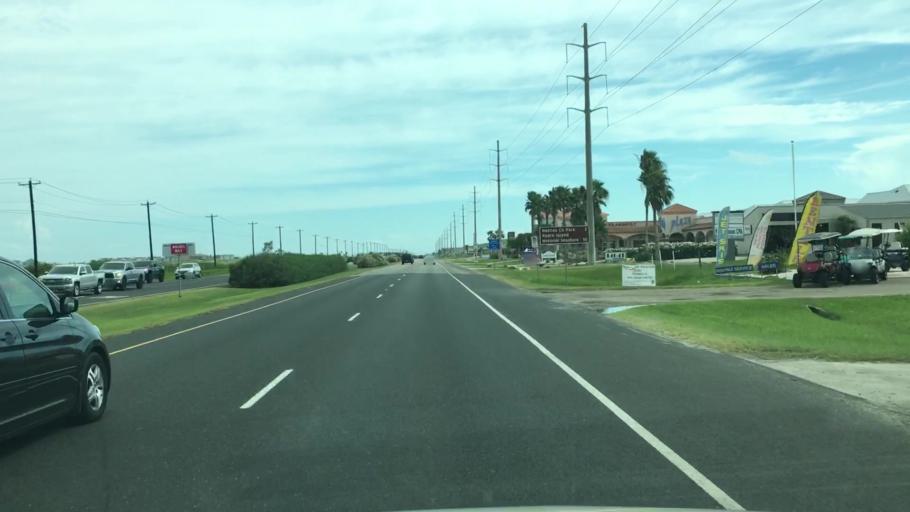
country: US
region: Texas
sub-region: Nueces County
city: Corpus Christi
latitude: 27.6175
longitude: -97.2219
